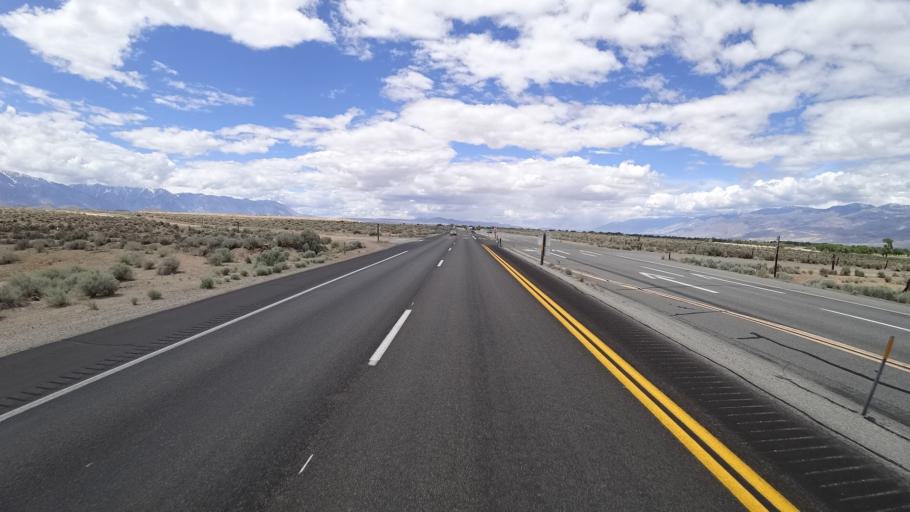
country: US
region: California
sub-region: Inyo County
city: Bishop
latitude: 37.3248
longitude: -118.3911
